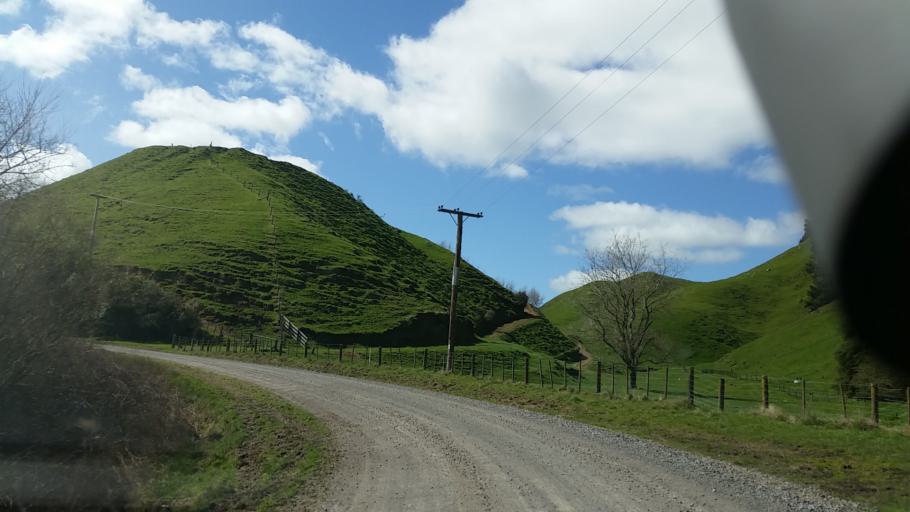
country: NZ
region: Waikato
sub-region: Taupo District
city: Taupo
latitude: -38.4804
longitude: 176.2164
